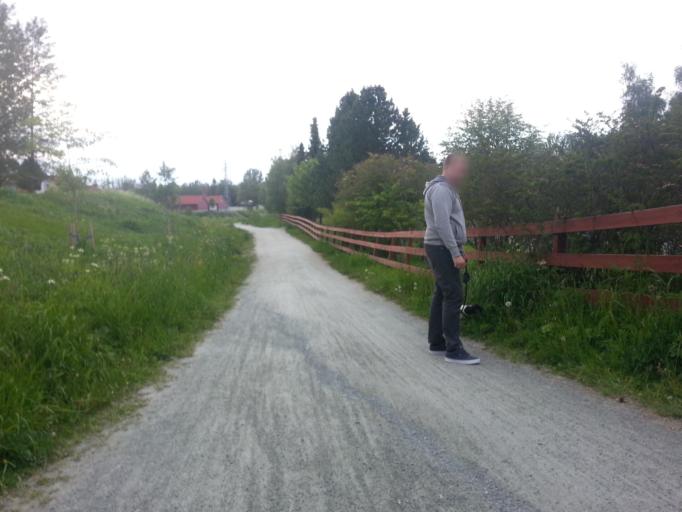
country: NO
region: Sor-Trondelag
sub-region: Trondheim
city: Trondheim
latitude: 63.4130
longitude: 10.4398
